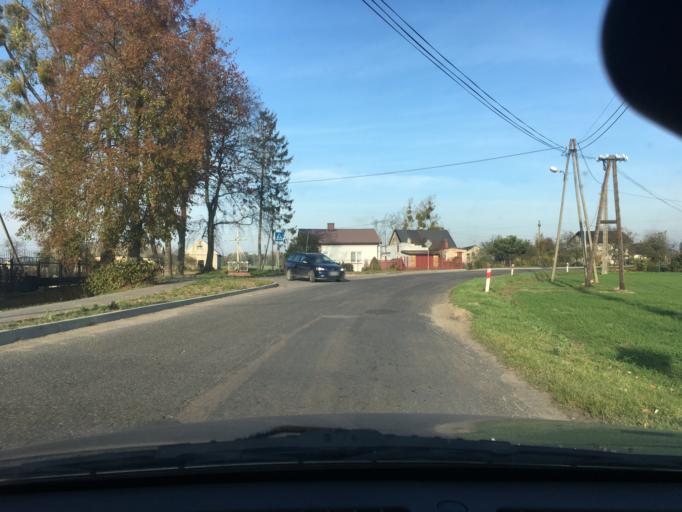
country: PL
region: Masovian Voivodeship
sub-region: Powiat plocki
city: Mala Wies
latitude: 52.4628
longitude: 20.1094
